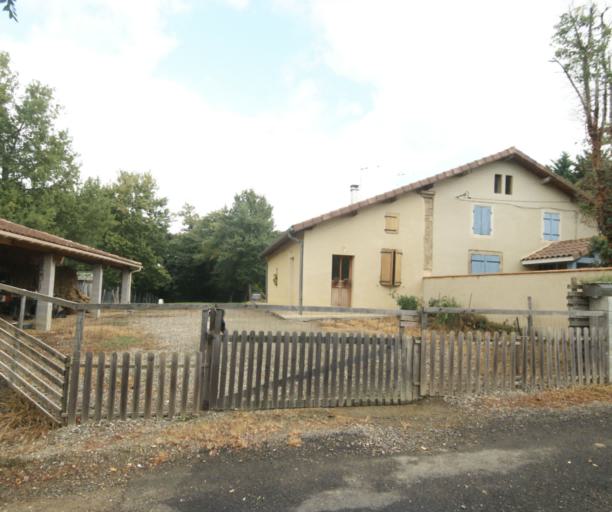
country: FR
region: Midi-Pyrenees
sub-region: Departement du Gers
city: Nogaro
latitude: 43.8169
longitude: -0.0781
